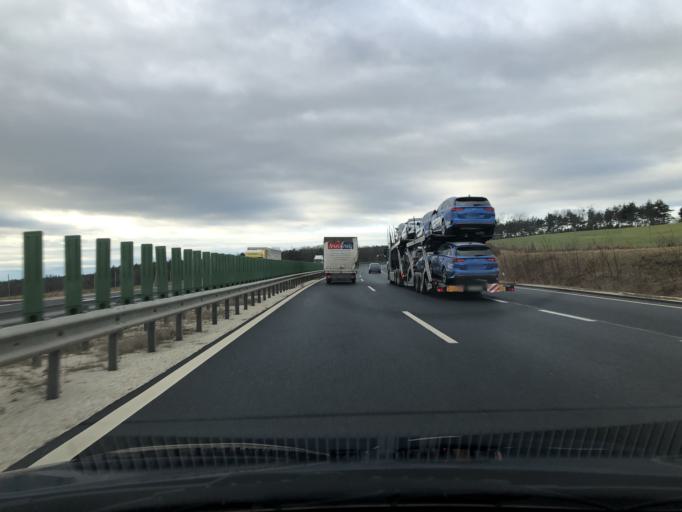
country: HU
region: Vas
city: Sarvar
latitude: 47.2995
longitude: 16.8353
